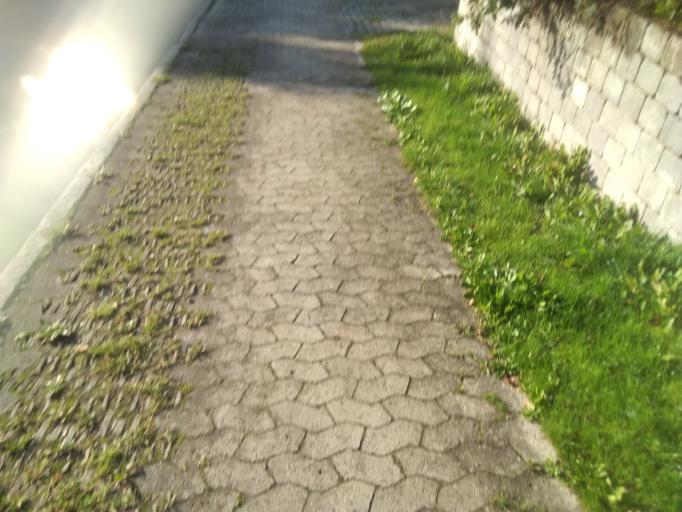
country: DK
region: Capital Region
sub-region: Gladsaxe Municipality
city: Buddinge
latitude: 55.7230
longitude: 12.5039
